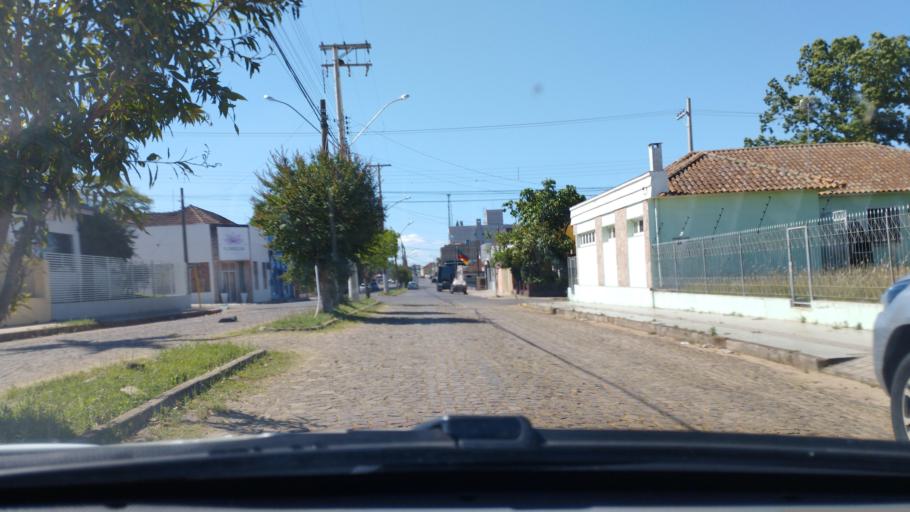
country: BR
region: Rio Grande do Sul
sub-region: Tupancireta
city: Tupancireta
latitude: -29.0873
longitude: -53.8349
